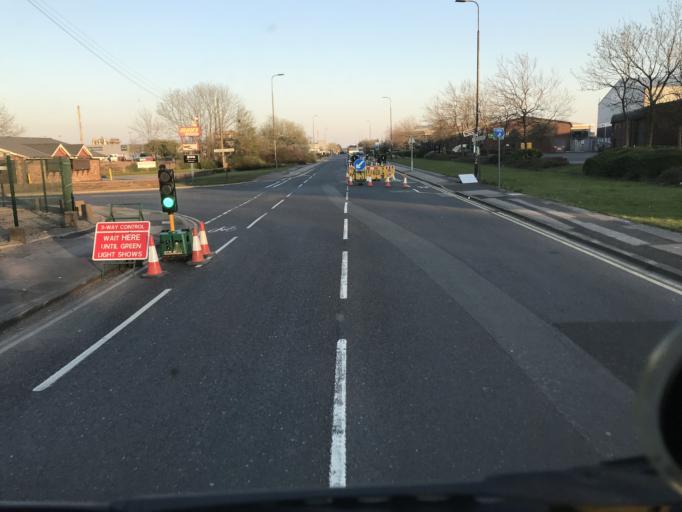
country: GB
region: England
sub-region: City and Borough of Salford
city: Eccles
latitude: 53.4734
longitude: -2.3351
